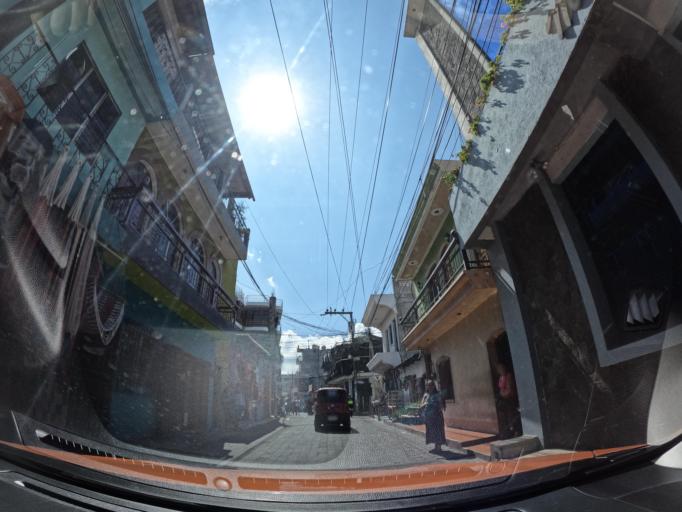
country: GT
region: Solola
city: Santiago Atitlan
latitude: 14.6397
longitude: -91.2311
